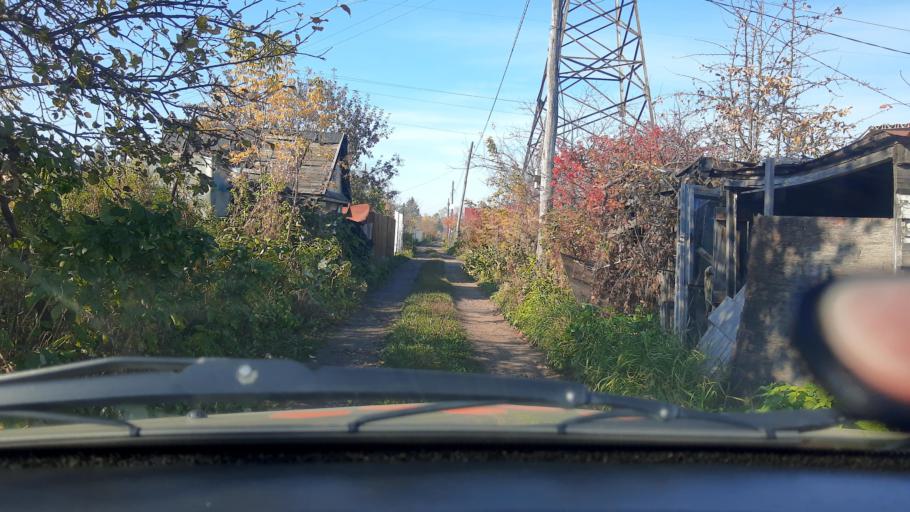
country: RU
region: Bashkortostan
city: Ufa
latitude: 54.8031
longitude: 56.1598
